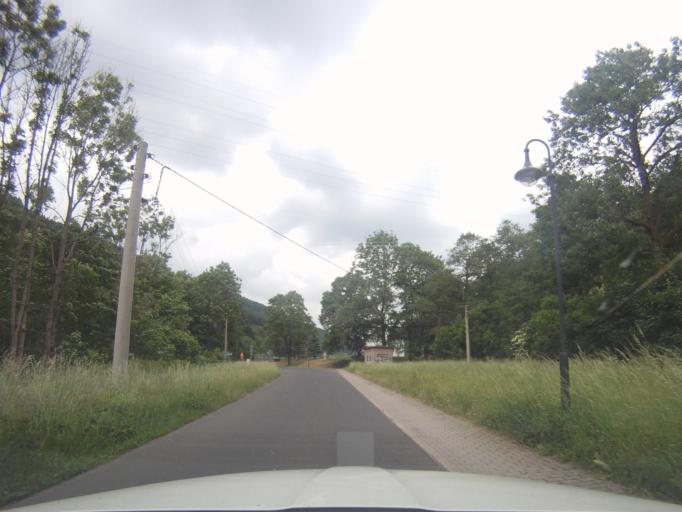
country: DE
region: Thuringia
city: Frauenwald
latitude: 50.5272
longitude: 10.8801
